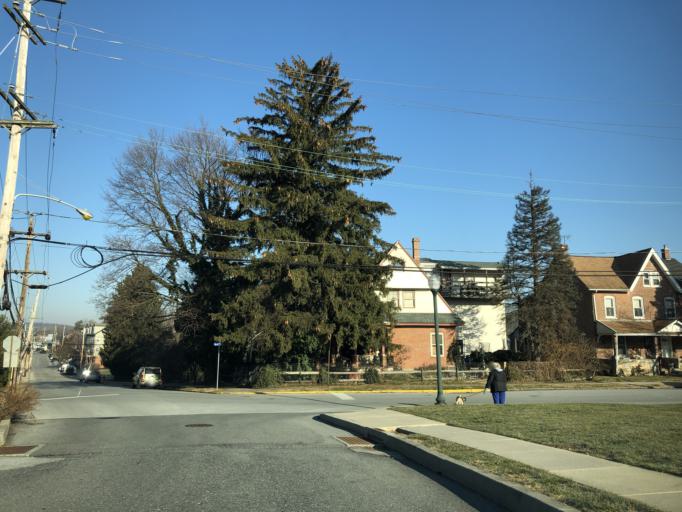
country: US
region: Pennsylvania
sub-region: Chester County
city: Downingtown
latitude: 40.0040
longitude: -75.6973
